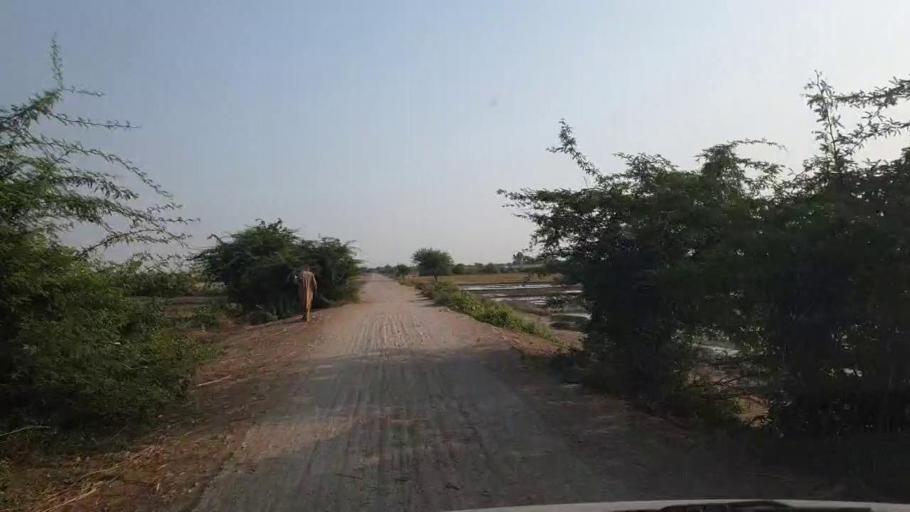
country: PK
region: Sindh
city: Rajo Khanani
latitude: 25.0213
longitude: 68.7823
